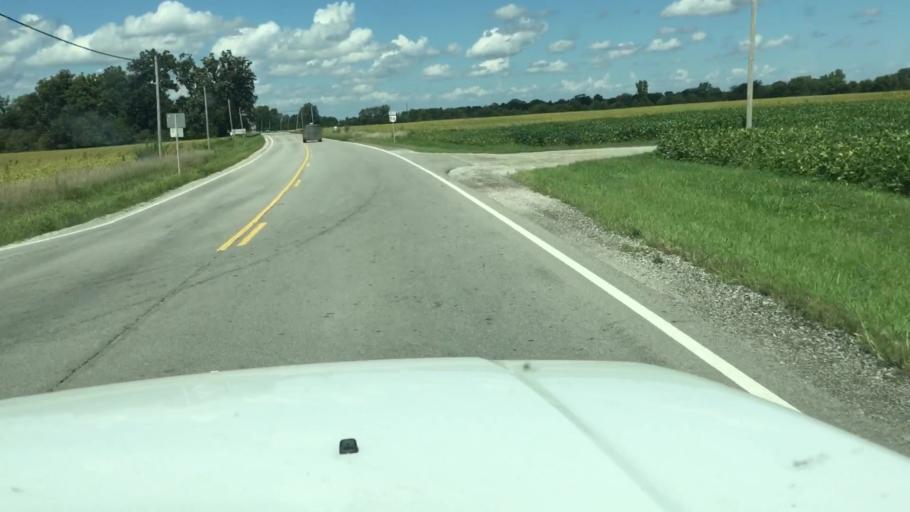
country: US
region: Ohio
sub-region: Madison County
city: Mount Sterling
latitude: 39.7302
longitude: -83.2714
